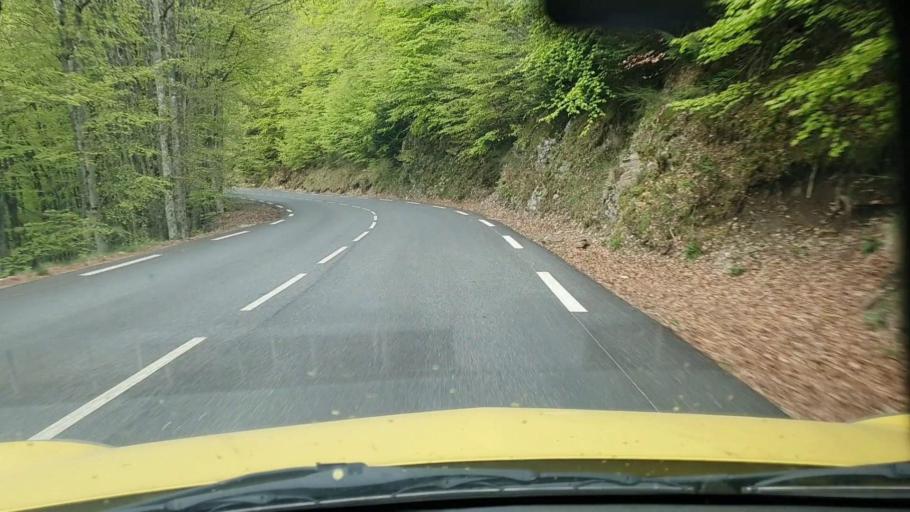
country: FR
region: Languedoc-Roussillon
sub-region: Departement du Gard
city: Valleraugue
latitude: 44.0934
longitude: 3.5576
